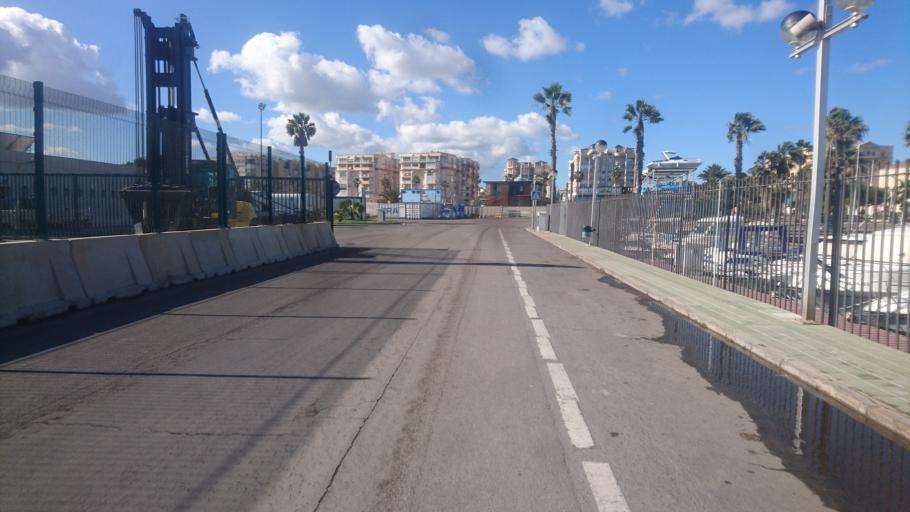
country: ES
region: Melilla
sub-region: Melilla
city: Melilla
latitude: 35.2878
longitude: -2.9349
